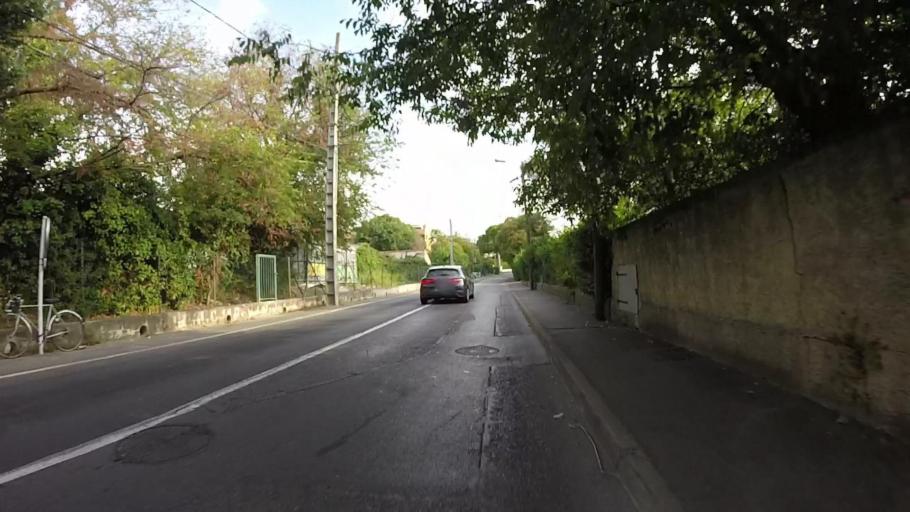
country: FR
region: Provence-Alpes-Cote d'Azur
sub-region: Departement des Alpes-Maritimes
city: Antibes
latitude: 43.5917
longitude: 7.1059
